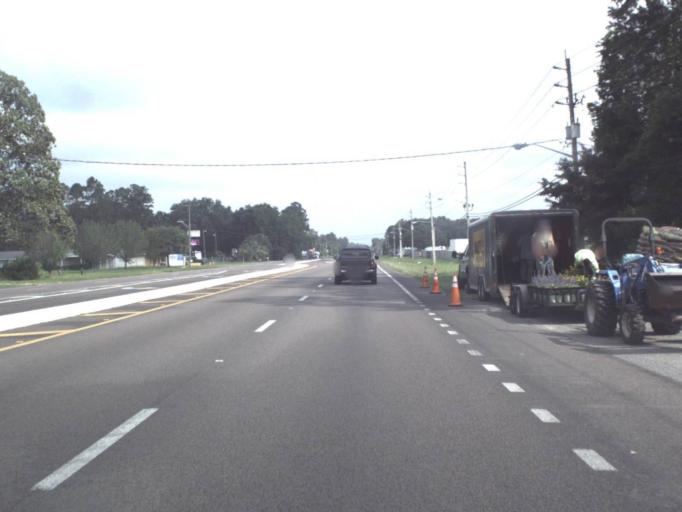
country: US
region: Florida
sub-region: Nassau County
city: Nassau Village-Ratliff
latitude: 30.4228
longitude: -81.7539
